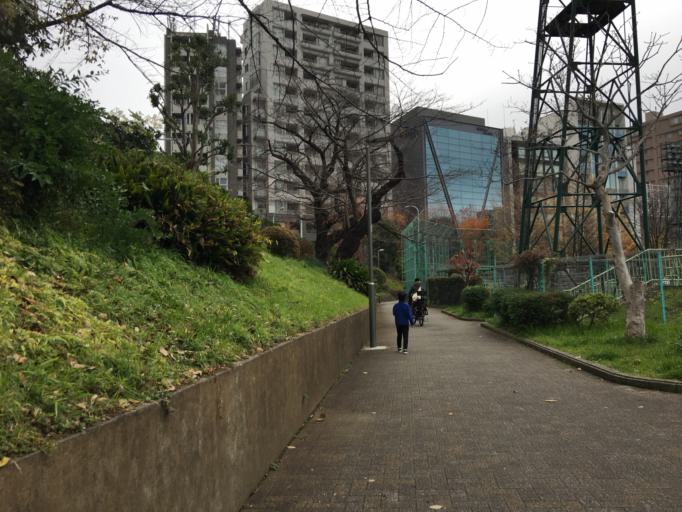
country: JP
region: Tokyo
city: Tokyo
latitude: 35.6891
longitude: 139.7308
